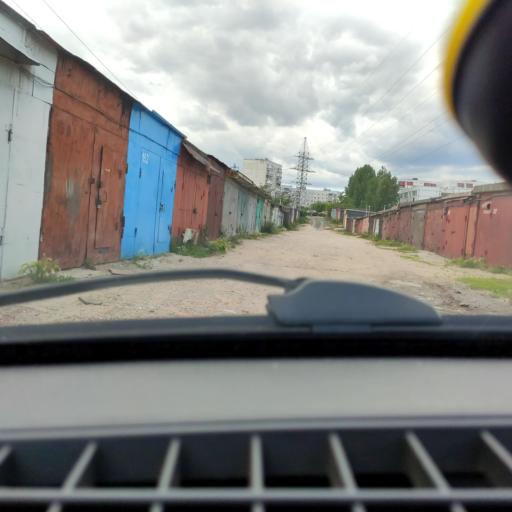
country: RU
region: Samara
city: Zhigulevsk
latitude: 53.4701
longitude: 49.5183
